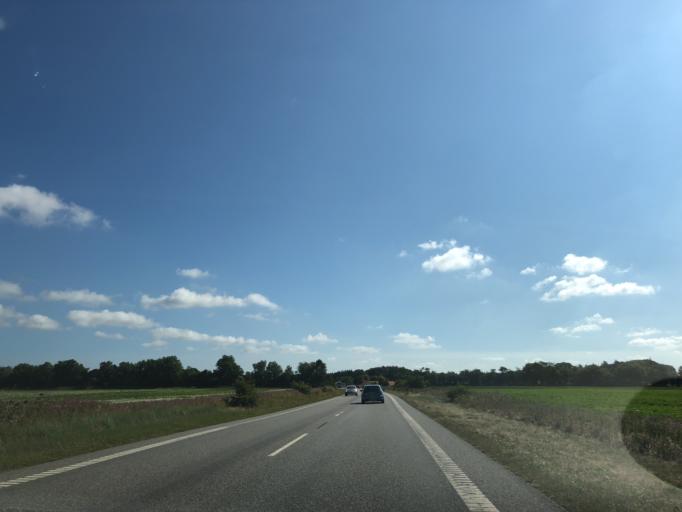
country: DK
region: North Denmark
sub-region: Jammerbugt Kommune
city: Fjerritslev
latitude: 57.0729
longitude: 9.2466
